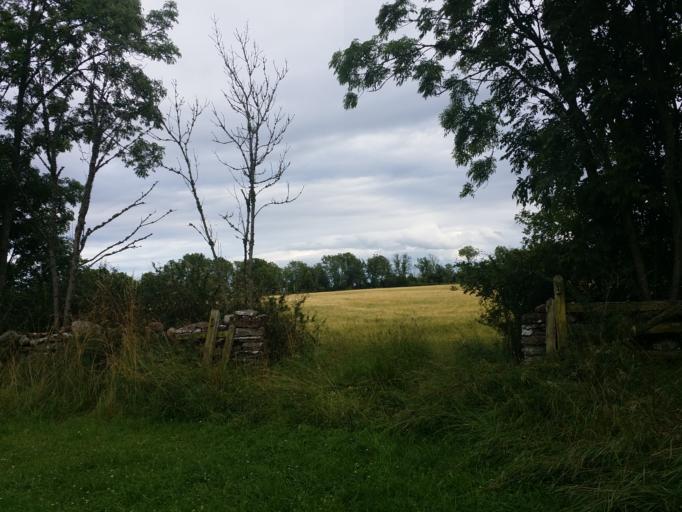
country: SE
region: Kalmar
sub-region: Borgholms Kommun
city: Borgholm
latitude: 57.1107
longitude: 16.9861
